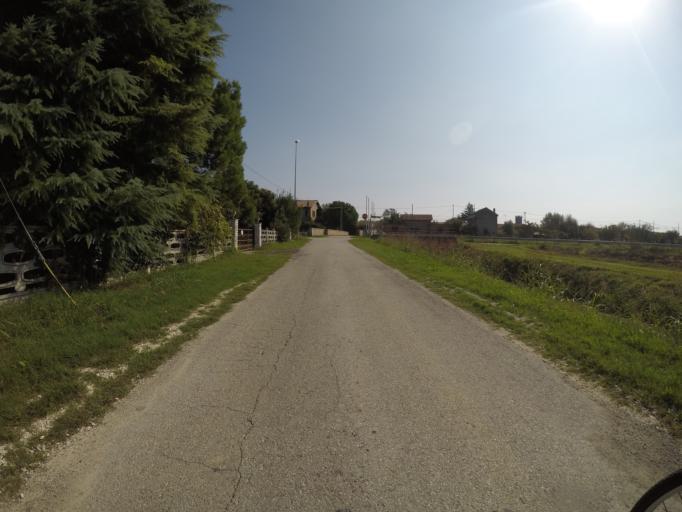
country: IT
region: Veneto
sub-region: Provincia di Rovigo
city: Polesella
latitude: 44.9652
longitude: 11.7394
